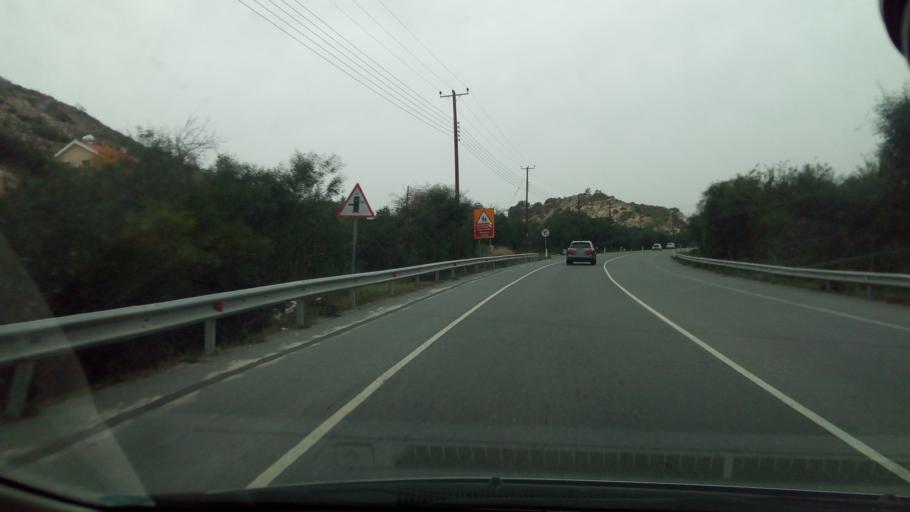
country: CY
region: Limassol
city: Pano Polemidia
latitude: 34.7362
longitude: 32.9866
